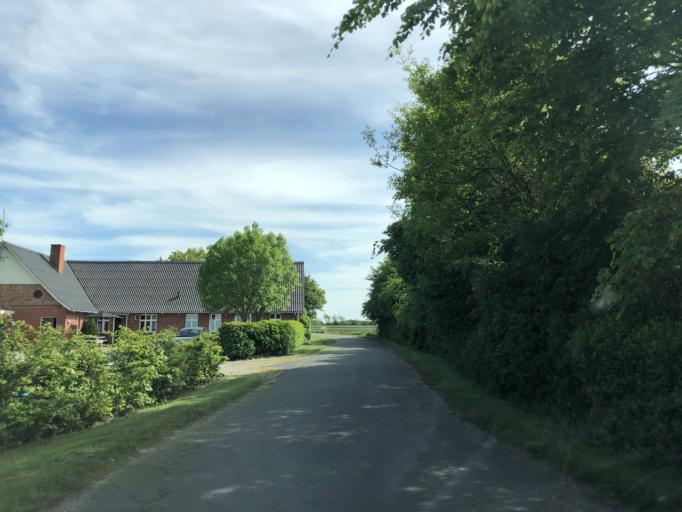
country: DK
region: Central Jutland
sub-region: Holstebro Kommune
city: Ulfborg
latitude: 56.2809
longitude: 8.2660
